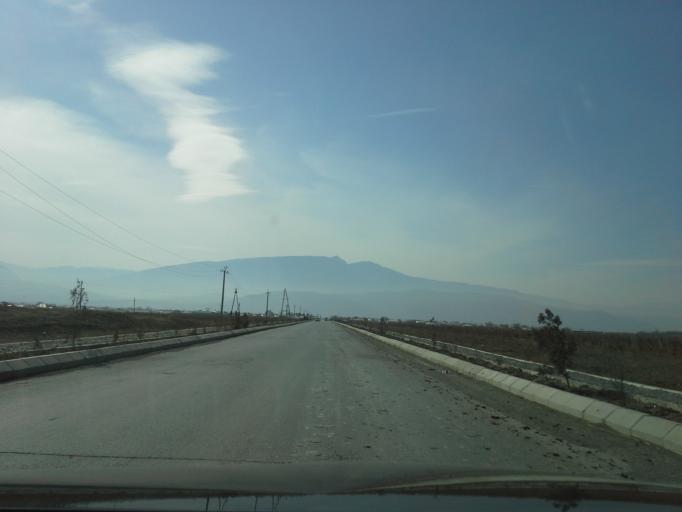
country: TM
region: Ahal
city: Abadan
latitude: 38.1198
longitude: 58.0406
